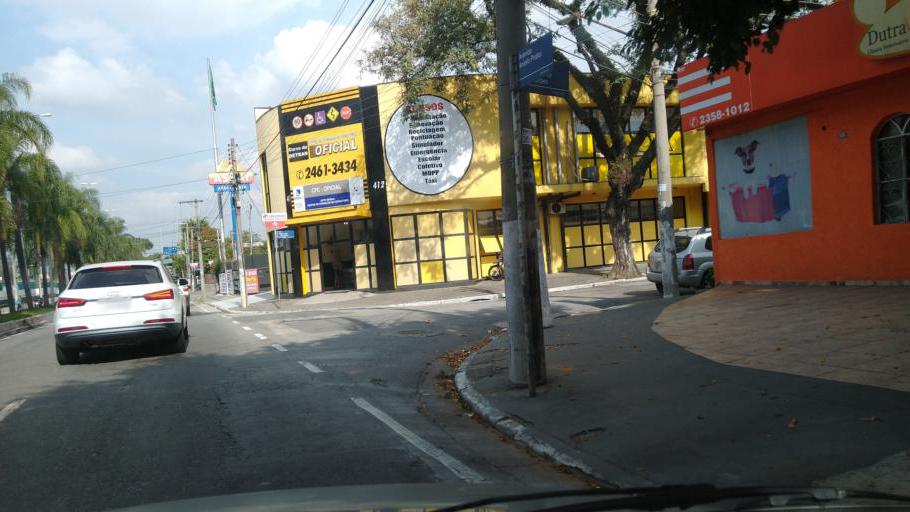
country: BR
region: Sao Paulo
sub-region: Guarulhos
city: Guarulhos
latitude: -23.4751
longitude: -46.5302
